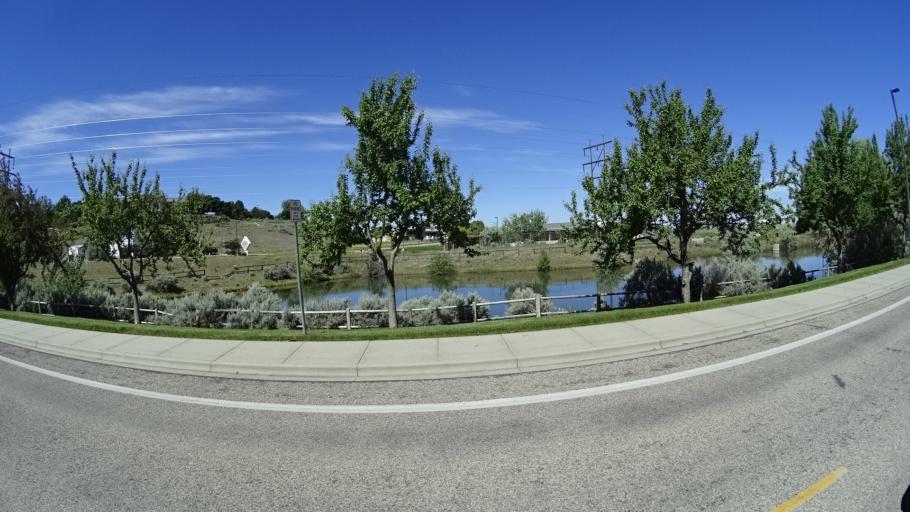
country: US
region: Idaho
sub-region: Ada County
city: Boise
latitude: 43.5468
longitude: -116.1535
